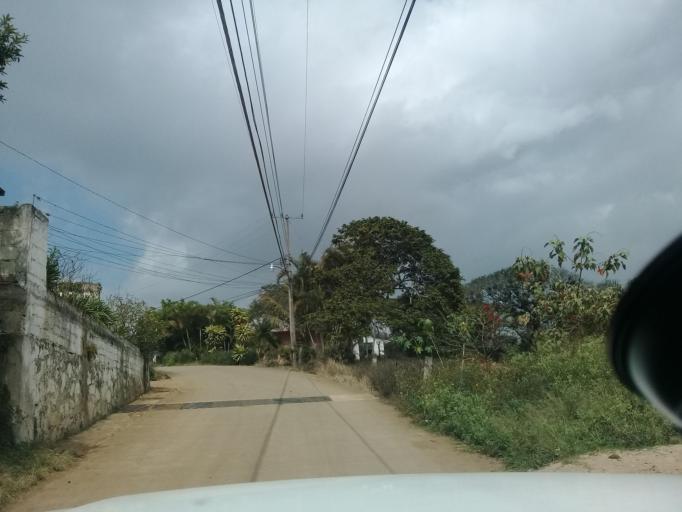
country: MX
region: Veracruz
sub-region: Xalapa
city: Fraccionamiento las Fuentes
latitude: 19.4771
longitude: -96.8757
